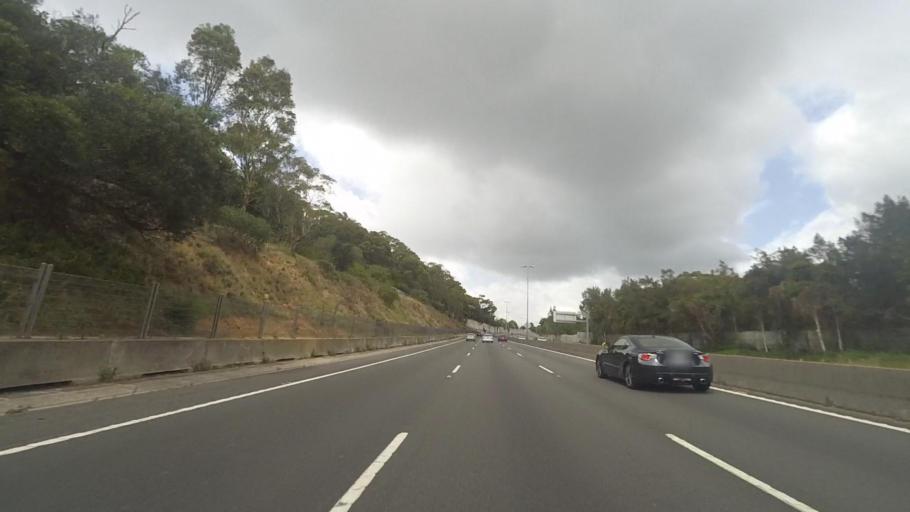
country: AU
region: New South Wales
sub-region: Wollongong
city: Gwynneville
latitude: -34.4160
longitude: 150.8798
